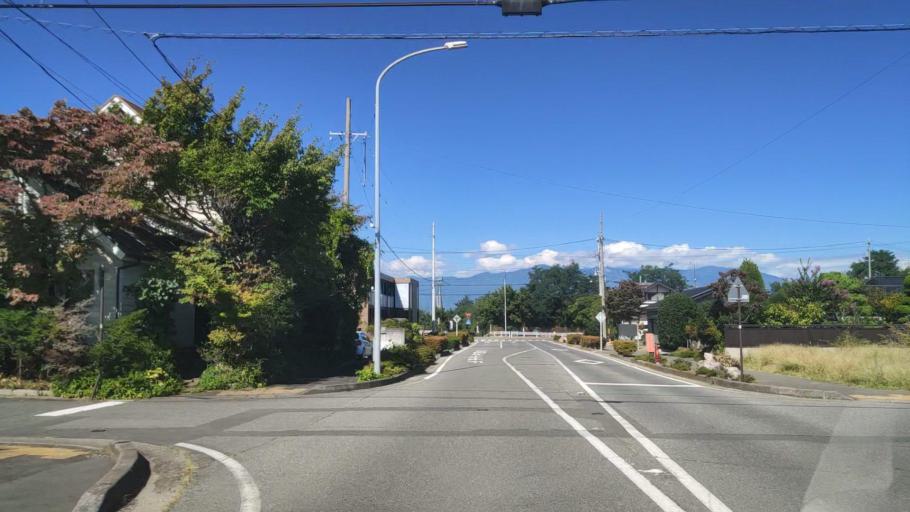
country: JP
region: Nagano
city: Shiojiri
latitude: 36.1591
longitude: 137.9452
